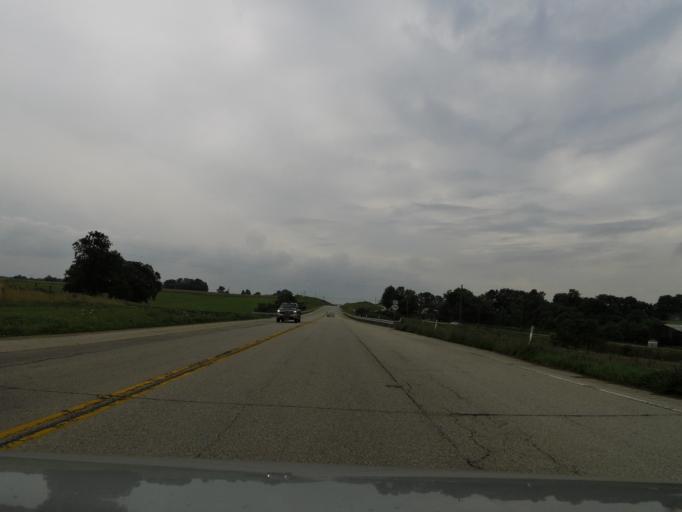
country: US
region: Kentucky
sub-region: Mason County
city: Maysville
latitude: 38.5515
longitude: -83.8231
